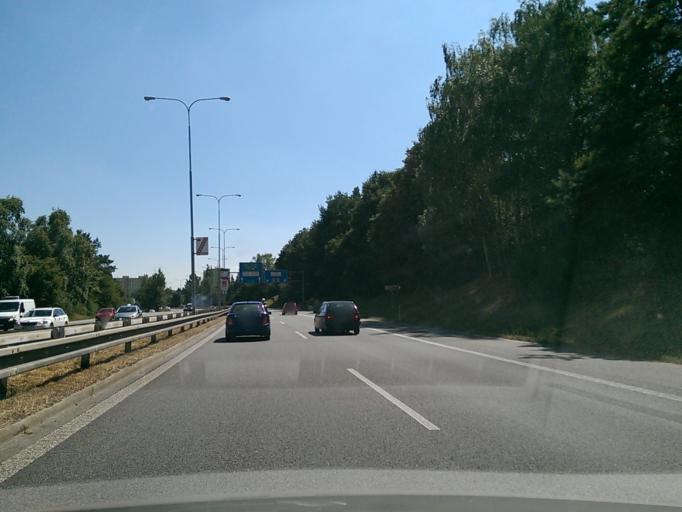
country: CZ
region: South Moravian
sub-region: Mesto Brno
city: Mokra Hora
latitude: 49.2405
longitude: 16.5890
